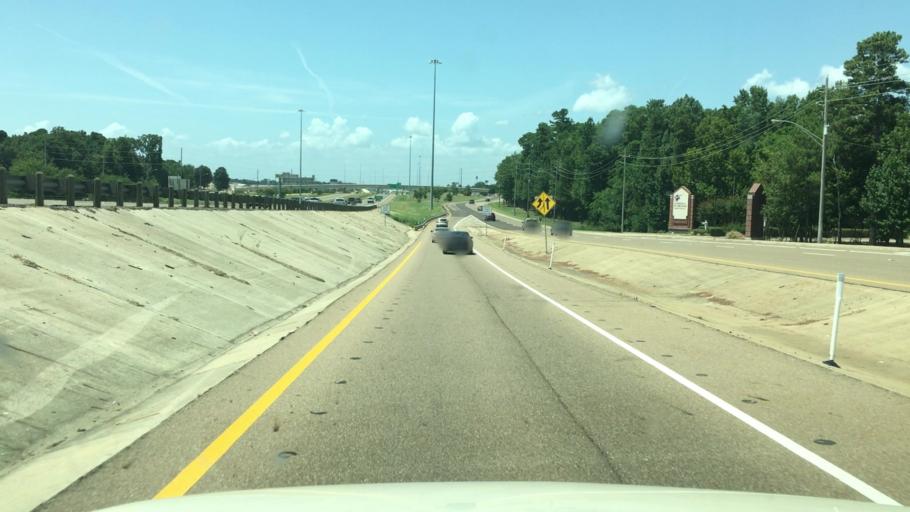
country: US
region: Arkansas
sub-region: Miller County
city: Texarkana
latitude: 33.4640
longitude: -94.0703
